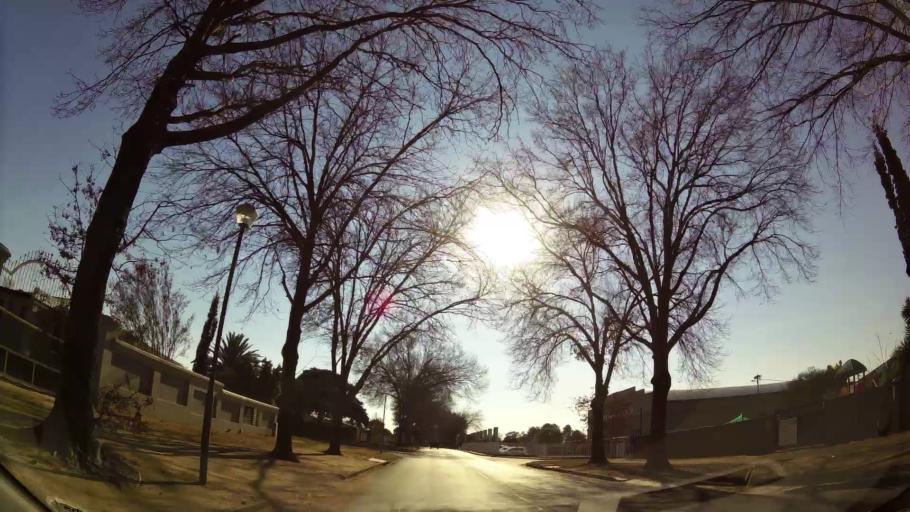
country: ZA
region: Gauteng
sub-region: Ekurhuleni Metropolitan Municipality
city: Benoni
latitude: -26.1624
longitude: 28.3142
